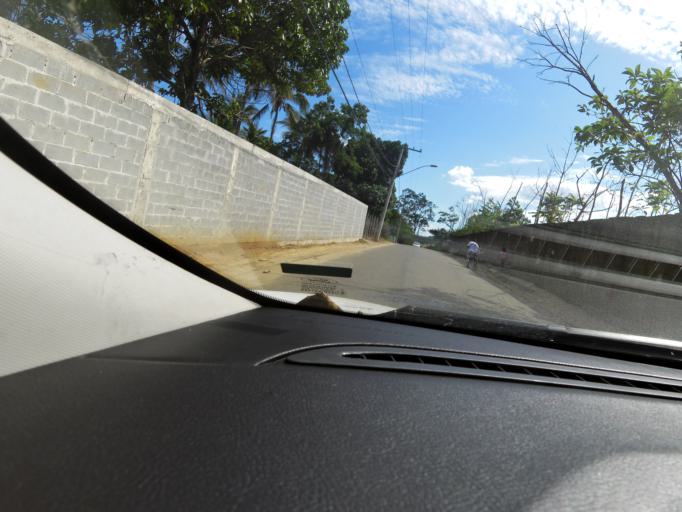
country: BR
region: Espirito Santo
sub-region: Guarapari
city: Guarapari
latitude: -20.6605
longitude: -40.5195
